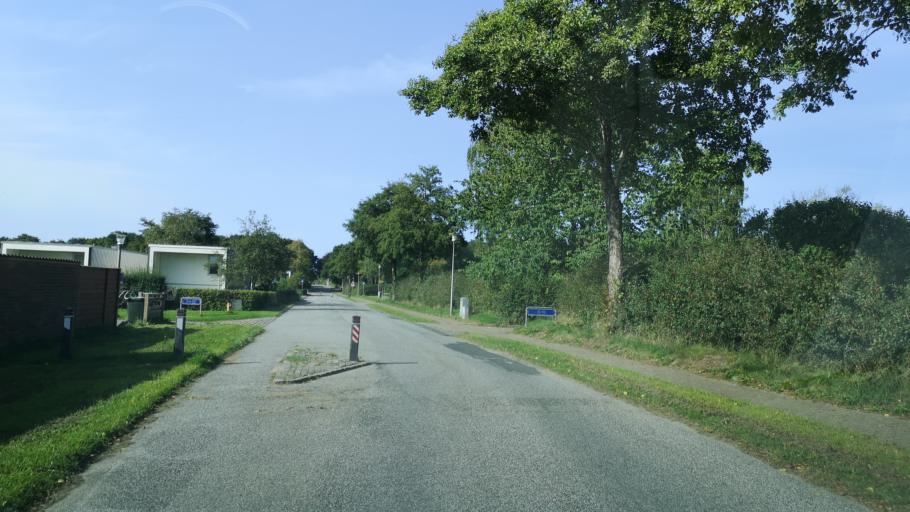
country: DK
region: Central Jutland
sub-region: Herning Kommune
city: Herning
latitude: 56.1672
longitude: 8.9762
